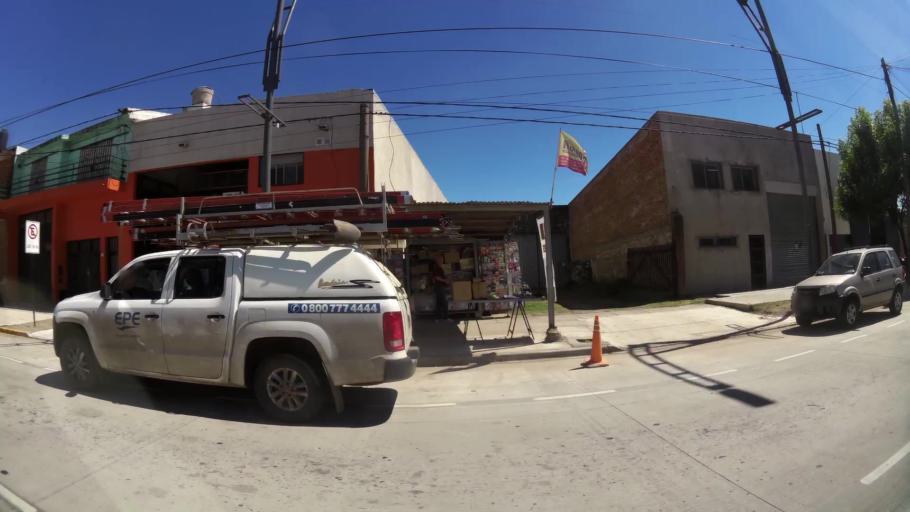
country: AR
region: Santa Fe
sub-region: Departamento de Rosario
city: Rosario
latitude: -32.9589
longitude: -60.7010
